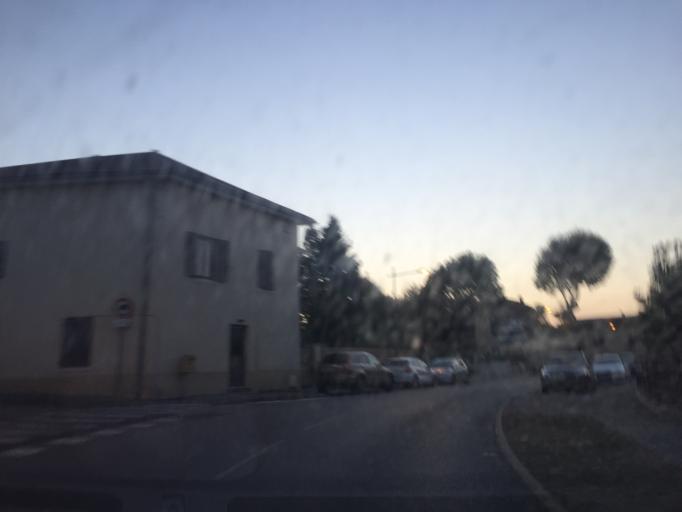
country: FR
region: Rhone-Alpes
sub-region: Departement de l'Ain
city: Mionnay
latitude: 45.8704
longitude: 4.9158
